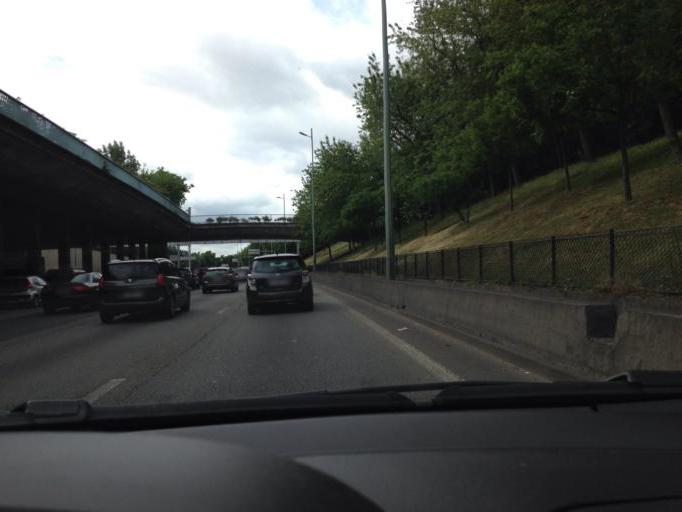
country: FR
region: Ile-de-France
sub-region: Departement des Hauts-de-Seine
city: Neuilly-sur-Seine
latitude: 48.8686
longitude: 2.2700
